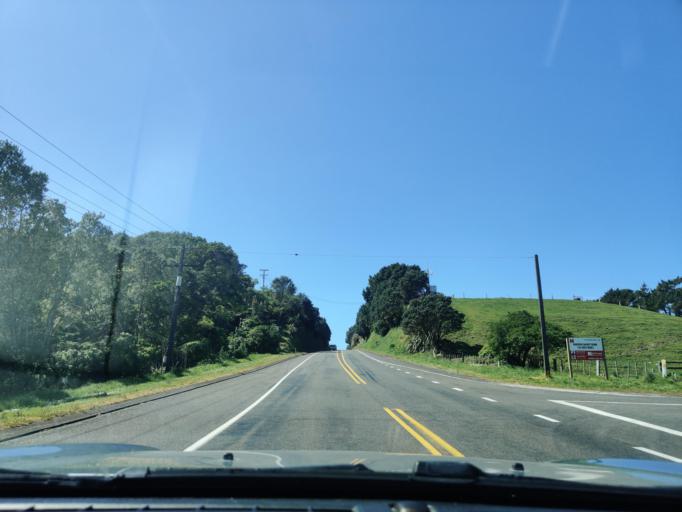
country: NZ
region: Taranaki
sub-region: New Plymouth District
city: New Plymouth
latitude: -39.1113
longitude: 173.9596
